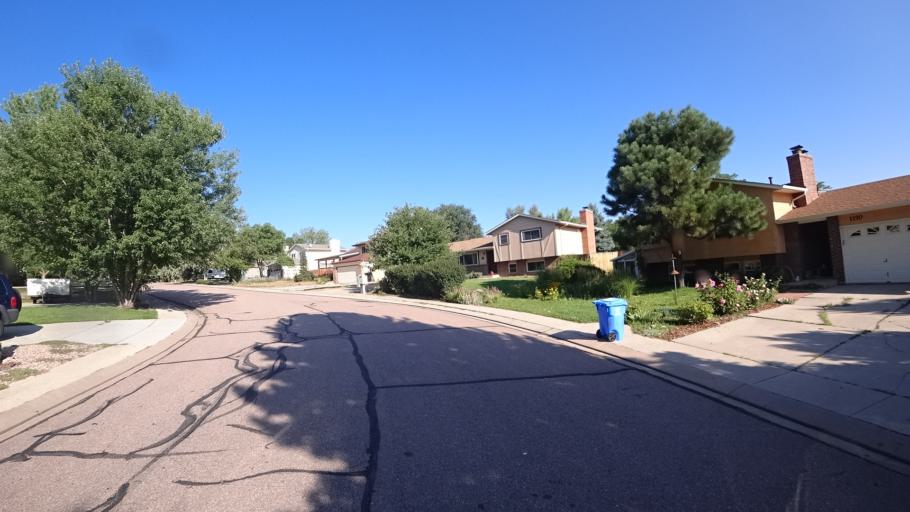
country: US
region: Colorado
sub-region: El Paso County
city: Colorado Springs
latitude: 38.8856
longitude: -104.8442
